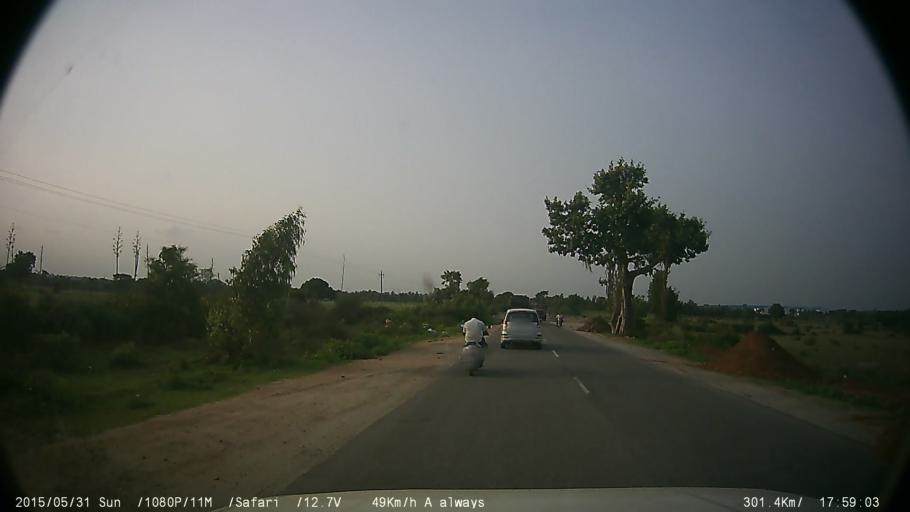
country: IN
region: Karnataka
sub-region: Mysore
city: Nanjangud
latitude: 12.0137
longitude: 76.6707
